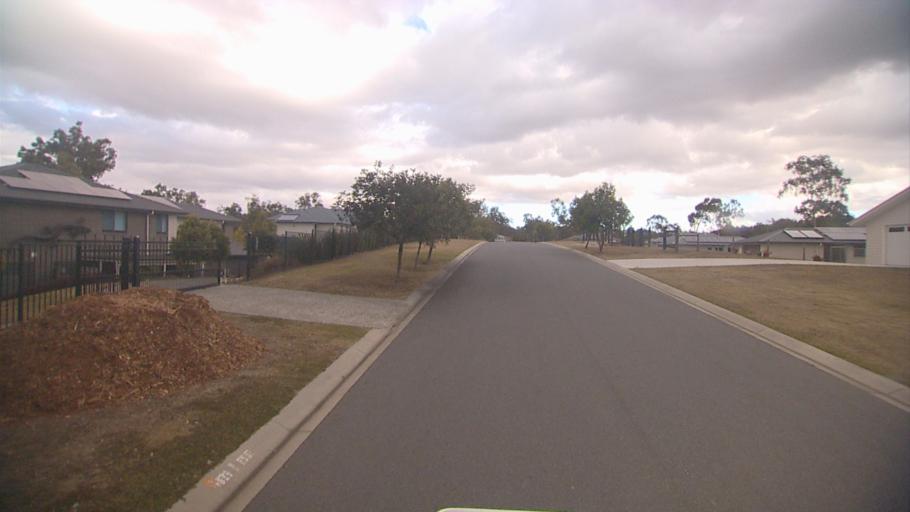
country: AU
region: Queensland
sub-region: Logan
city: Cedar Vale
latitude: -27.8637
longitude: 153.0771
